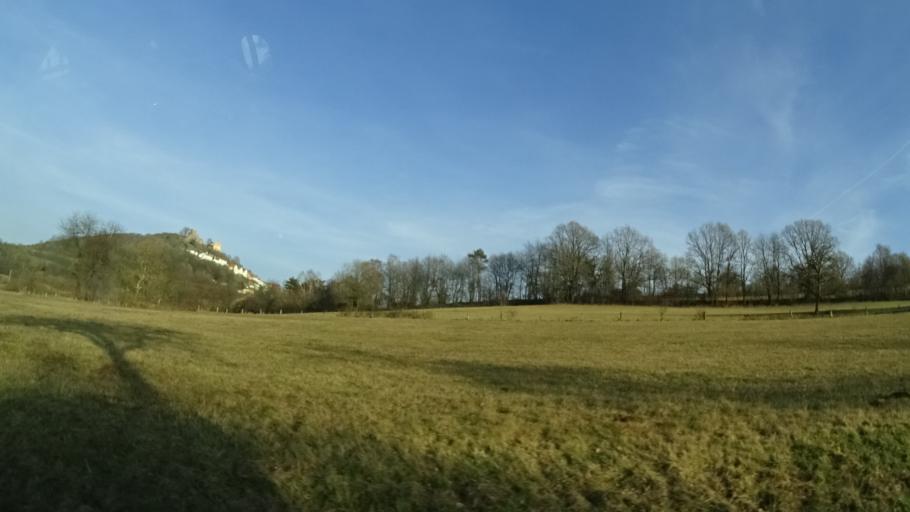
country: DE
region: Bavaria
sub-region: Regierungsbezirk Unterfranken
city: Zeitlofs
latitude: 50.2974
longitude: 9.6609
